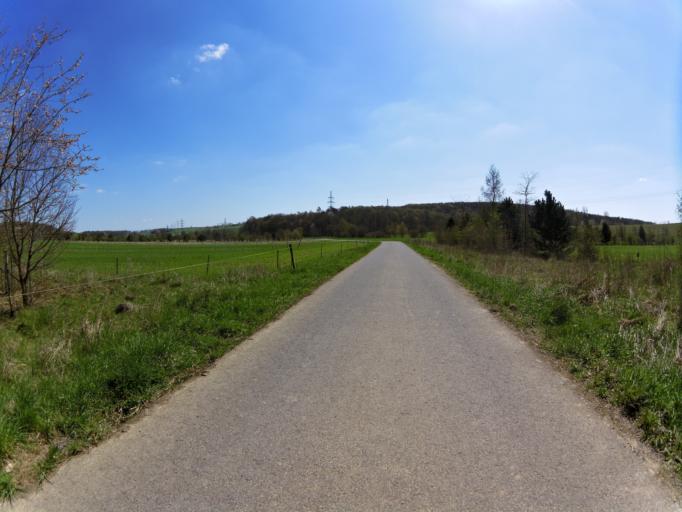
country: DE
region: Bavaria
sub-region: Regierungsbezirk Unterfranken
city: Hettstadt
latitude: 49.8139
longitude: 9.7954
